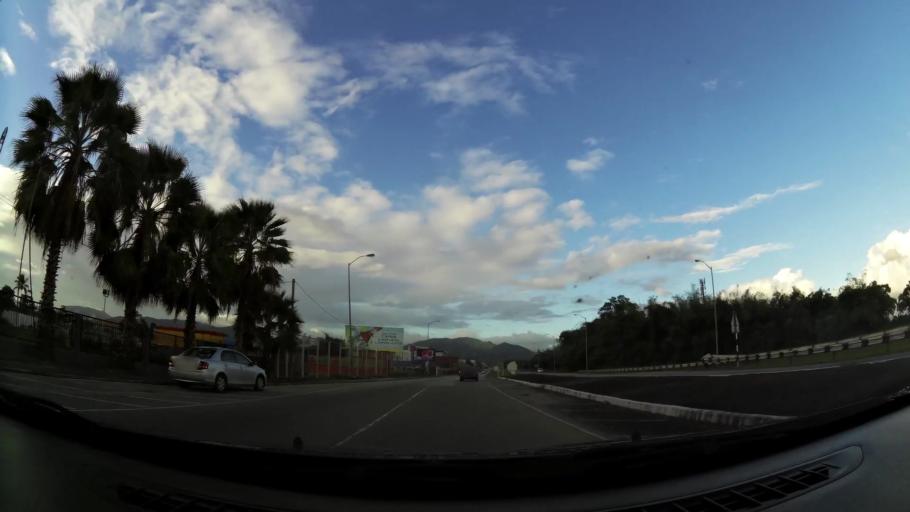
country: TT
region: Tunapuna/Piarco
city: Arouca
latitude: 10.6048
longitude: -61.3450
